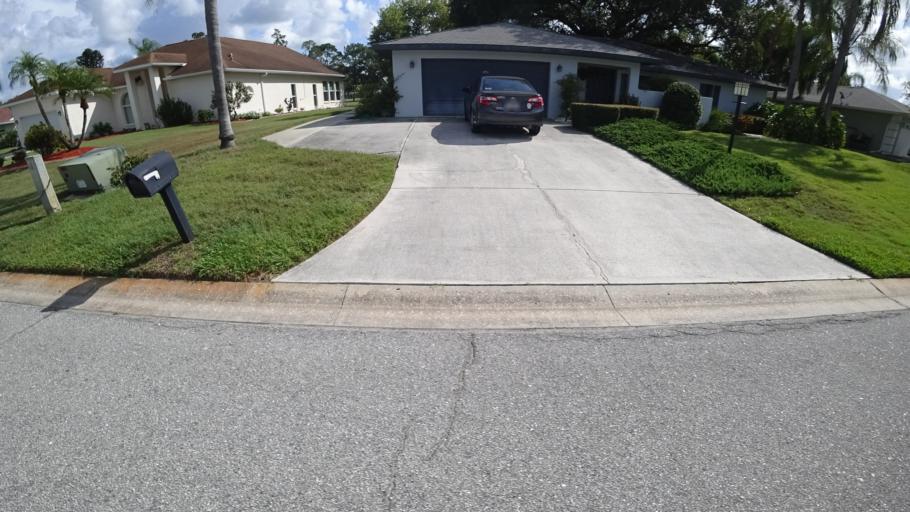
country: US
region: Florida
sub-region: Sarasota County
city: Desoto Lakes
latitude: 27.3996
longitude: -82.4962
